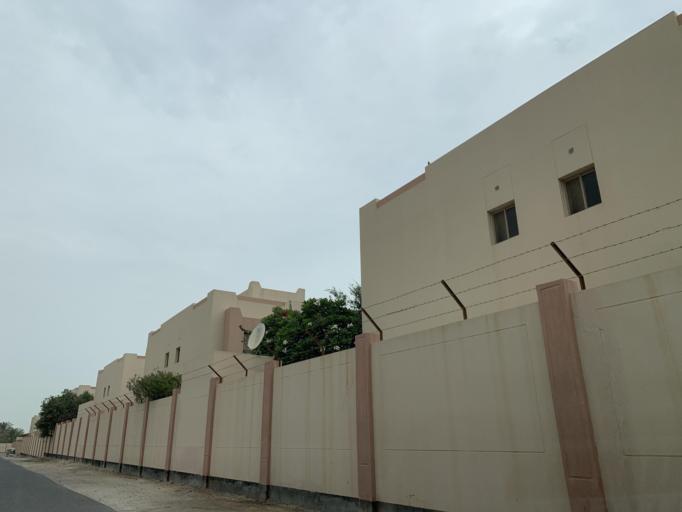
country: BH
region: Northern
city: Madinat `Isa
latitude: 26.1890
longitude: 50.4728
